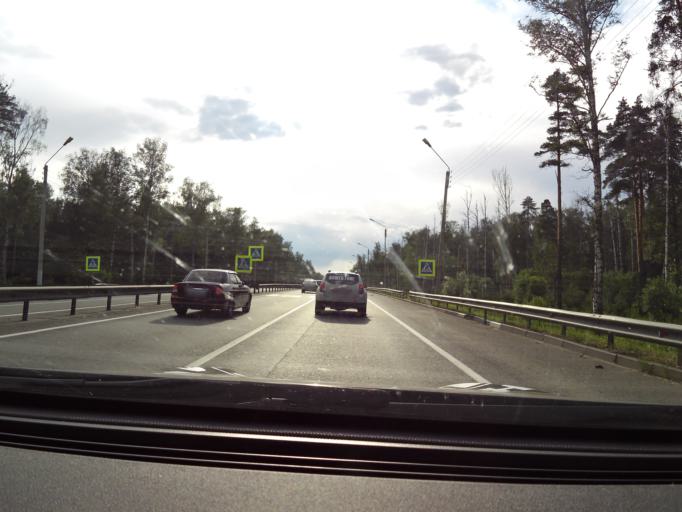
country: RU
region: Vladimir
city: Novovyazniki
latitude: 56.2202
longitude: 42.1699
